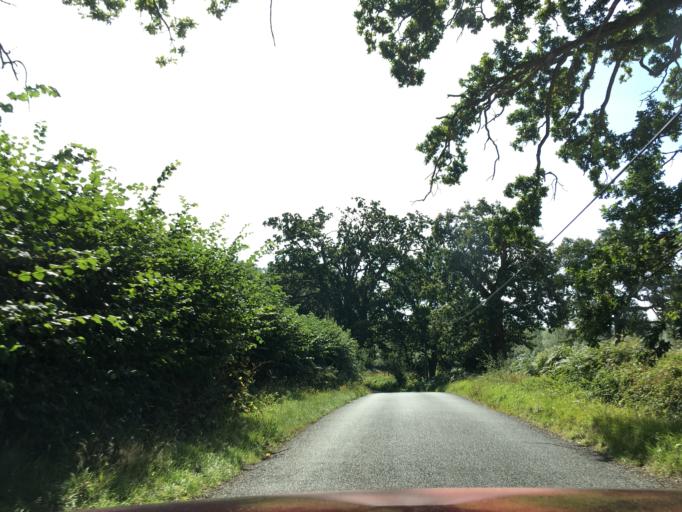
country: GB
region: England
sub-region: West Berkshire
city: Kintbury
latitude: 51.3737
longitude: -1.4388
